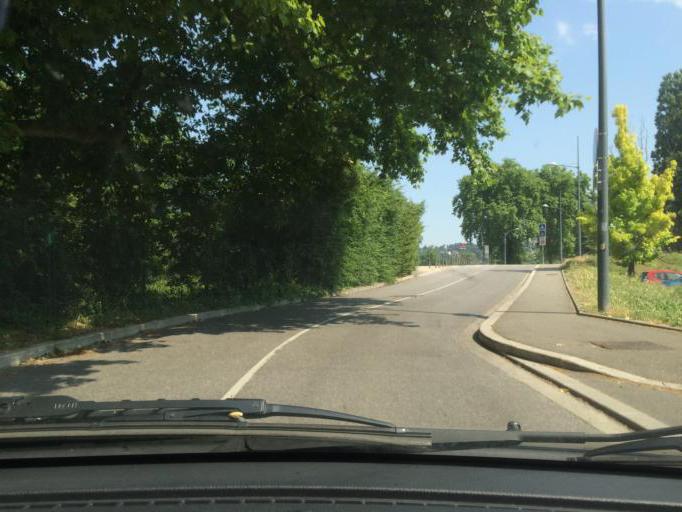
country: FR
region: Rhone-Alpes
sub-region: Departement du Rhone
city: Villeurbanne
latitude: 45.7799
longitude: 4.8648
